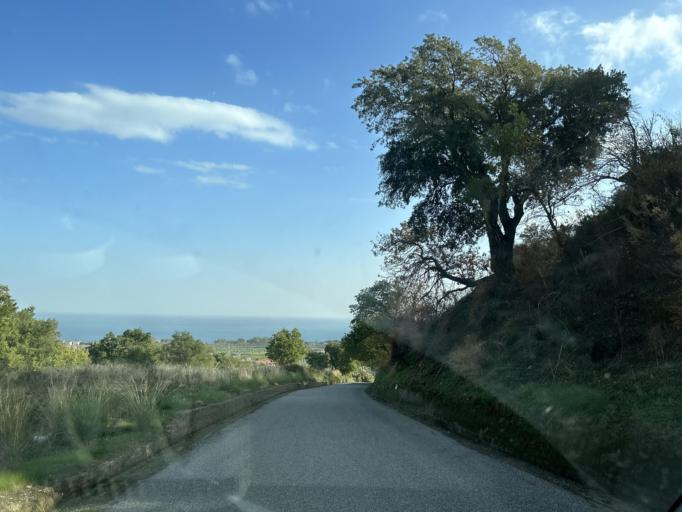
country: IT
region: Calabria
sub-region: Provincia di Catanzaro
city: Montepaone
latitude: 38.7173
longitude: 16.5154
